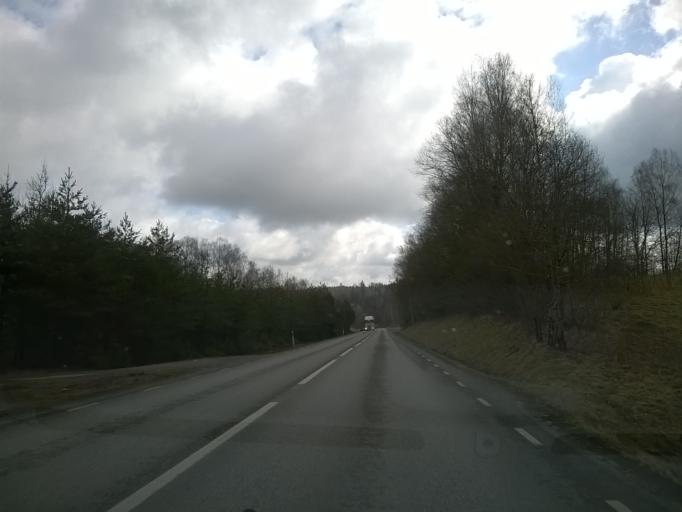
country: SE
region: Halland
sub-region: Varbergs Kommun
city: Tvaaker
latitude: 57.1478
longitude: 12.6056
